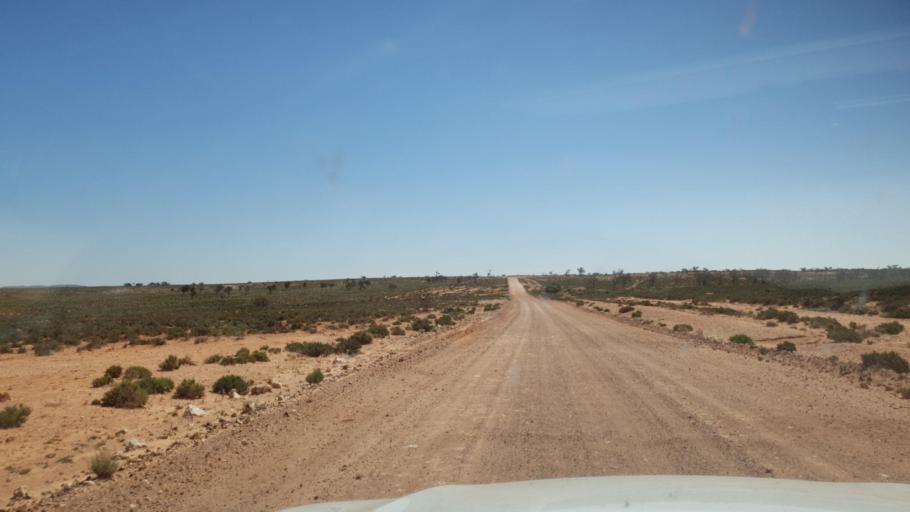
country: AU
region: South Australia
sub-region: Whyalla
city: Whyalla
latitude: -32.6506
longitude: 136.9743
